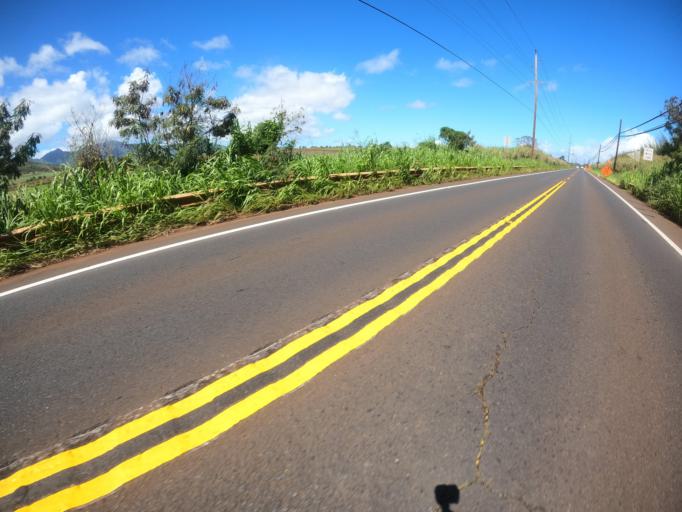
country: US
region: Hawaii
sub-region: Honolulu County
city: Schofield Barracks
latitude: 21.4668
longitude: -158.0545
